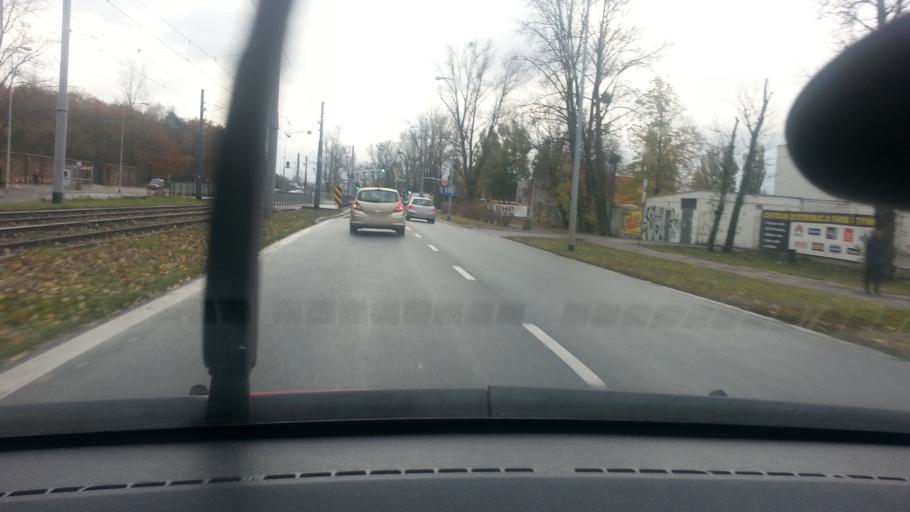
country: PL
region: Masovian Voivodeship
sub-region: Warszawa
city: Praga Polnoc
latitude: 52.2744
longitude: 21.0309
